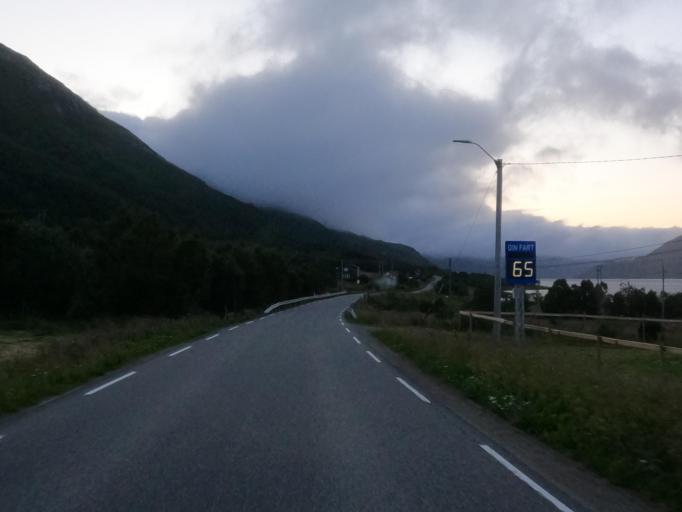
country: NO
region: Nordland
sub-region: Lodingen
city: Lodingen
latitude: 68.5701
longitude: 15.7966
